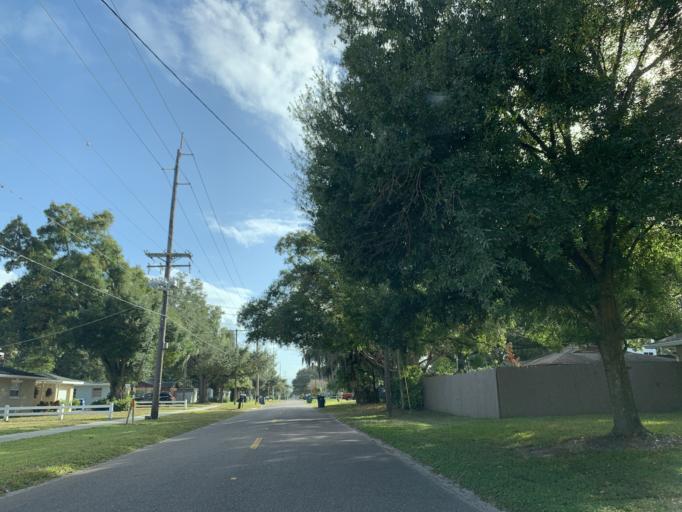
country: US
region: Florida
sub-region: Hillsborough County
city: Tampa
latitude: 27.9041
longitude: -82.5123
